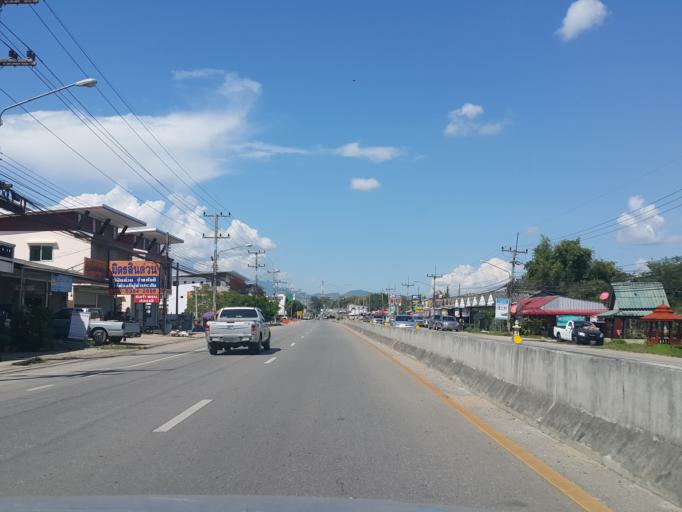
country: TH
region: Chiang Mai
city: Mae Taeng
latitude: 19.0873
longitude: 98.9369
